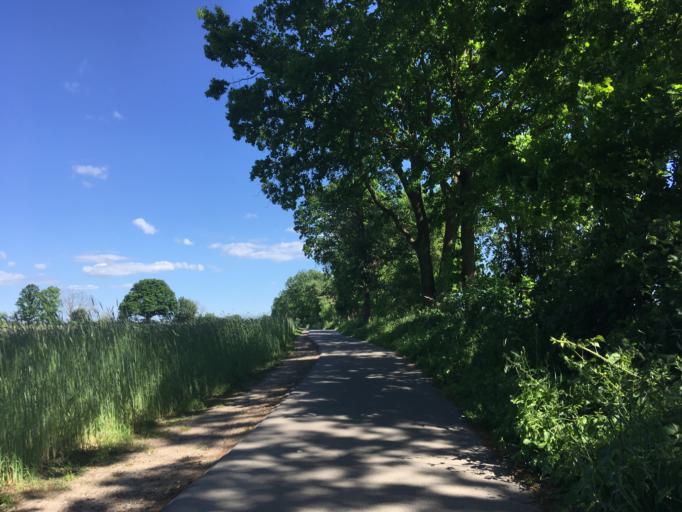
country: DE
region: Brandenburg
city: Althuttendorf
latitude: 52.9841
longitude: 13.8100
